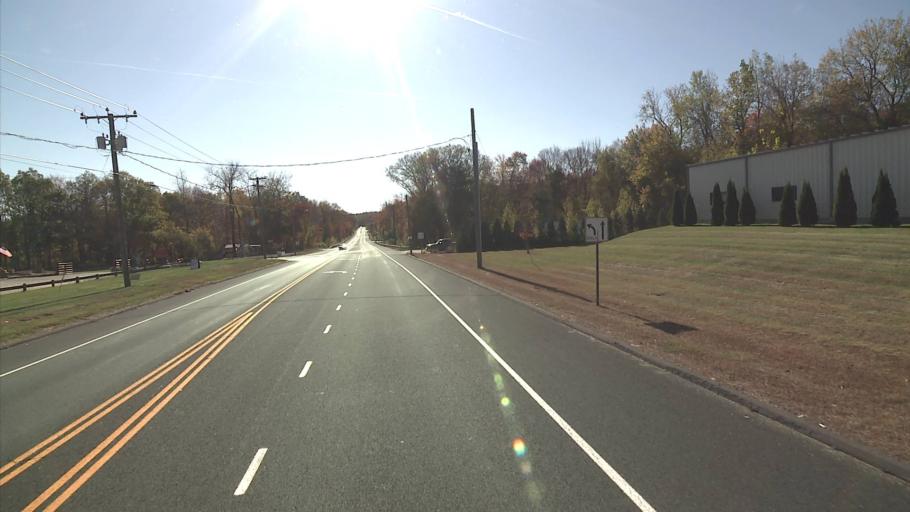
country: US
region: Connecticut
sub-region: Tolland County
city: Coventry Lake
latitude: 41.7575
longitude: -72.4012
